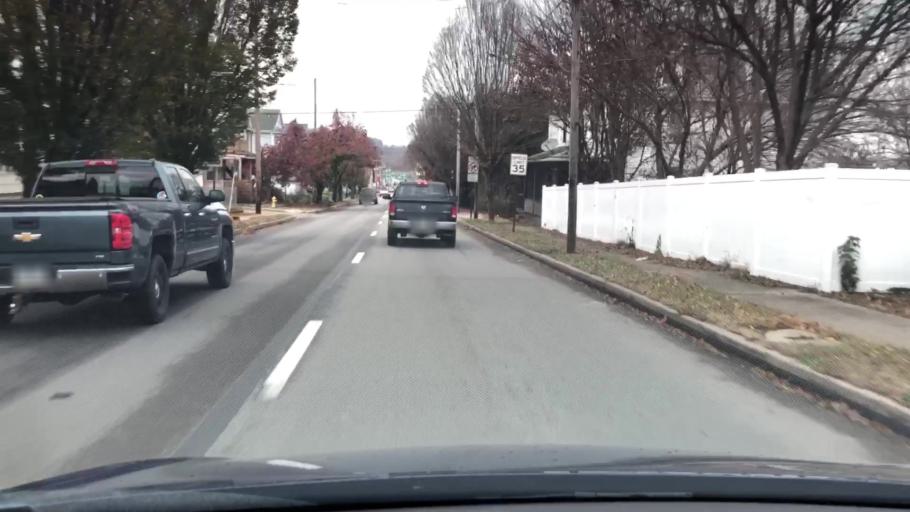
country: US
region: Pennsylvania
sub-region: Fayette County
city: Connellsville
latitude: 40.0131
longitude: -79.5988
